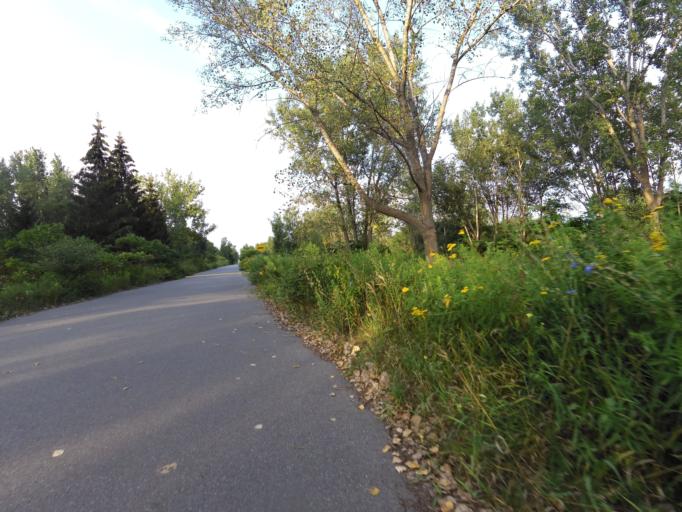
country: CA
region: Ontario
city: Toronto
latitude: 43.6209
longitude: -79.3385
